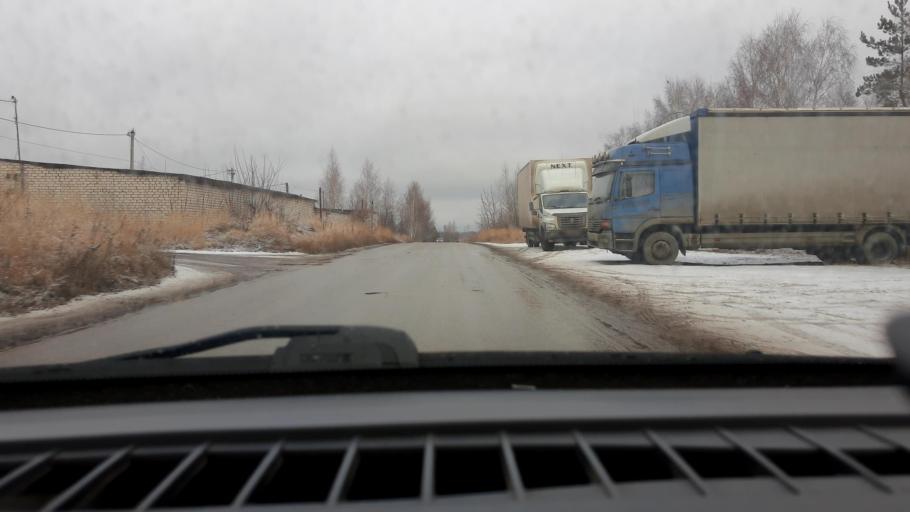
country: RU
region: Nizjnij Novgorod
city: Taremskoye
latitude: 55.9370
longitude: 43.0597
